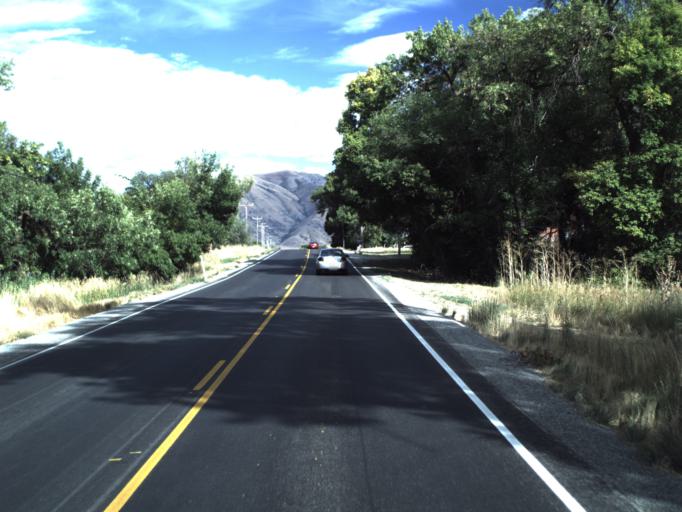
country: US
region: Utah
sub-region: Cache County
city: Wellsville
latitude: 41.6411
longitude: -111.8941
